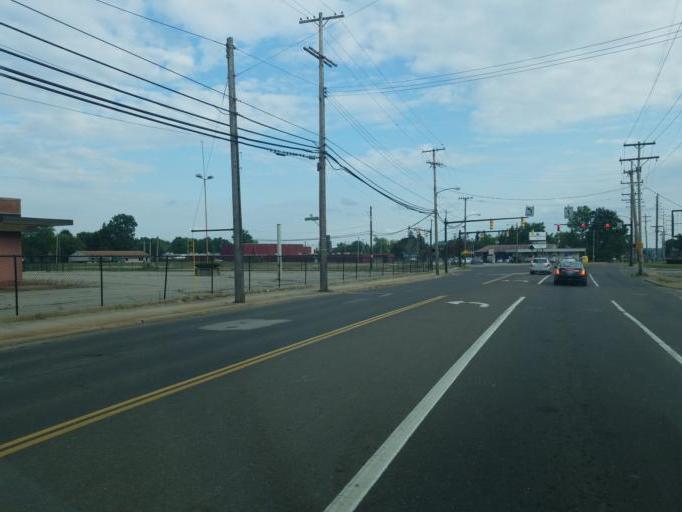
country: US
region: Ohio
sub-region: Mahoning County
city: Youngstown
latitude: 41.1254
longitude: -80.6641
